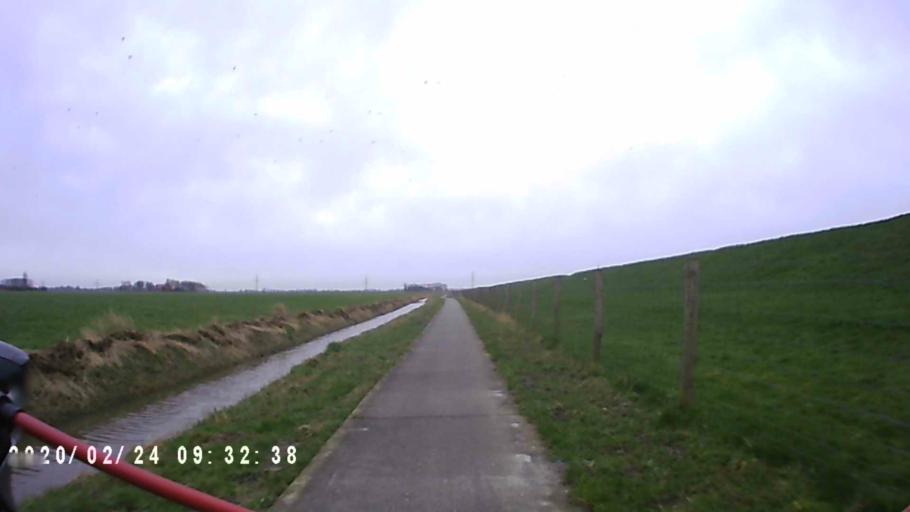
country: NL
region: Groningen
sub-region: Gemeente Winsum
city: Winsum
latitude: 53.3037
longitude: 6.4974
